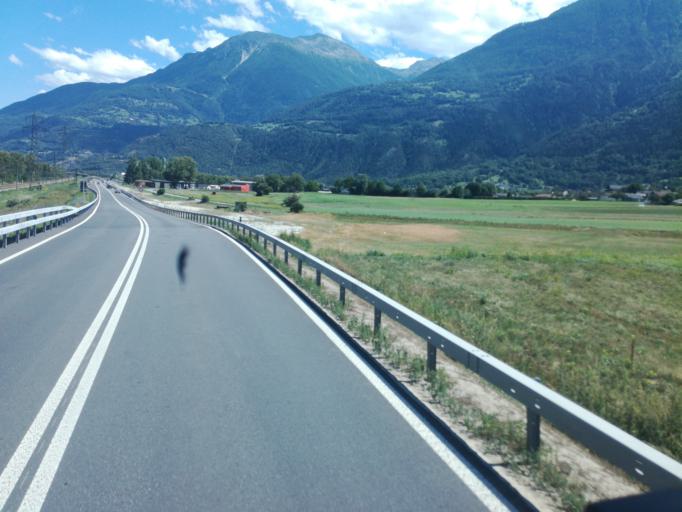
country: CH
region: Valais
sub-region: Leuk District
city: Leuk
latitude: 46.3087
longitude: 7.6535
